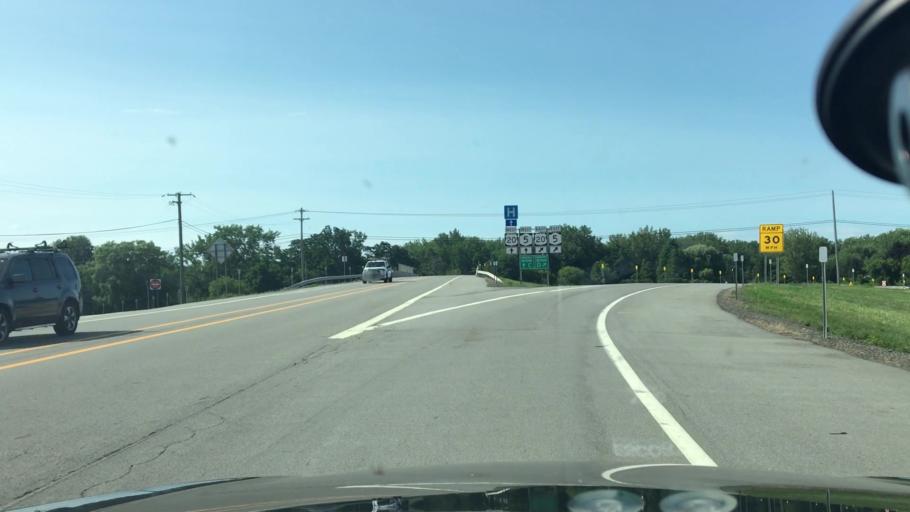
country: US
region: New York
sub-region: Chautauqua County
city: Silver Creek
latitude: 42.5613
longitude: -79.1160
